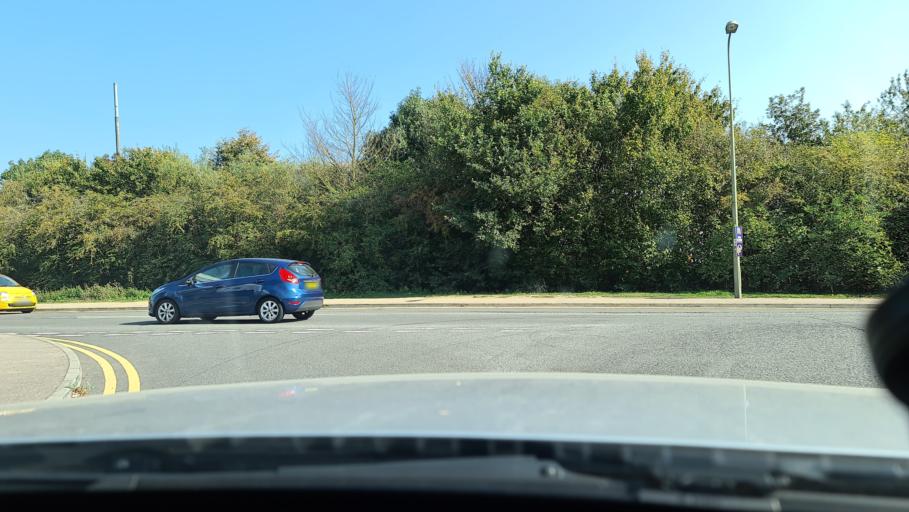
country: GB
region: England
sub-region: Oxfordshire
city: Banbury
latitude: 52.0757
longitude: -1.3187
